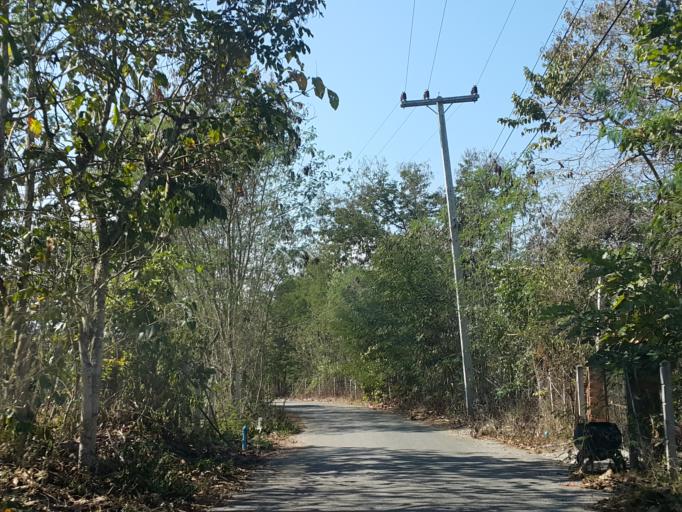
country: TH
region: Chiang Mai
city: Mae Taeng
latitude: 19.0363
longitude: 98.9852
